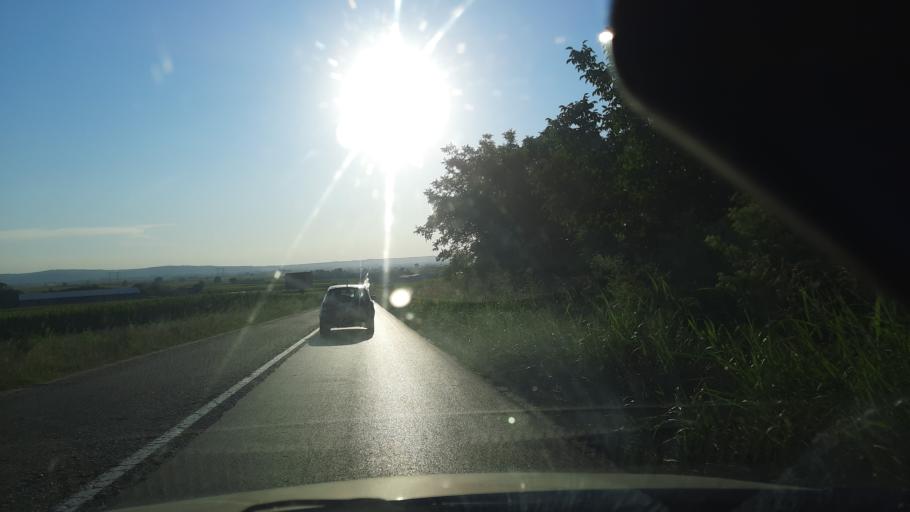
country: RS
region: Central Serbia
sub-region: Branicevski Okrug
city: Malo Crnice
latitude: 44.5736
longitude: 21.3567
